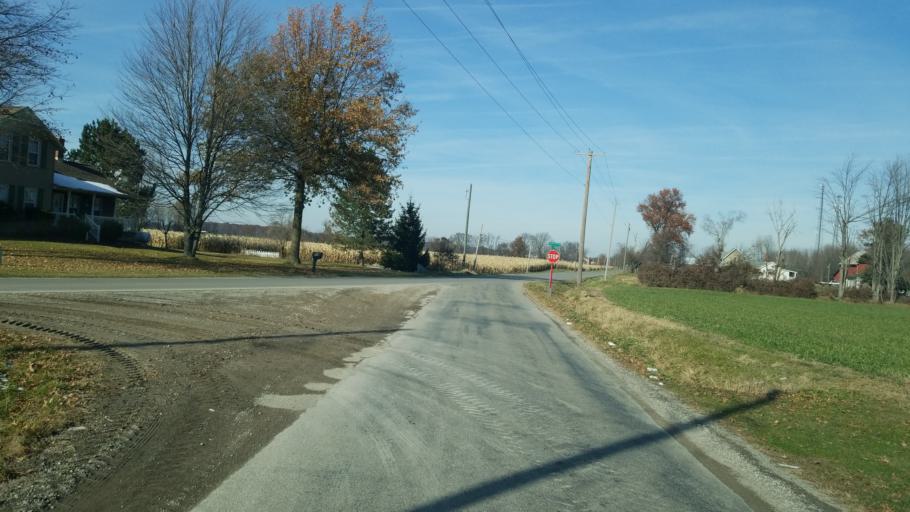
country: US
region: Ohio
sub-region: Huron County
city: Wakeman
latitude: 41.2388
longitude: -82.4216
